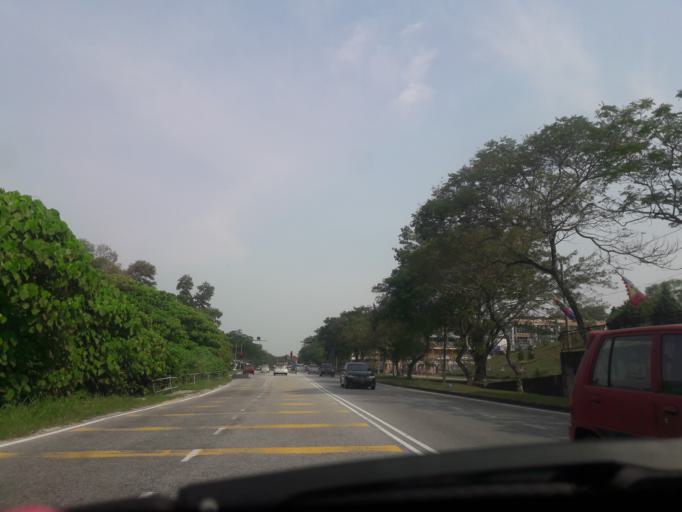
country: MY
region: Kedah
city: Kulim
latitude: 5.3680
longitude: 100.5448
